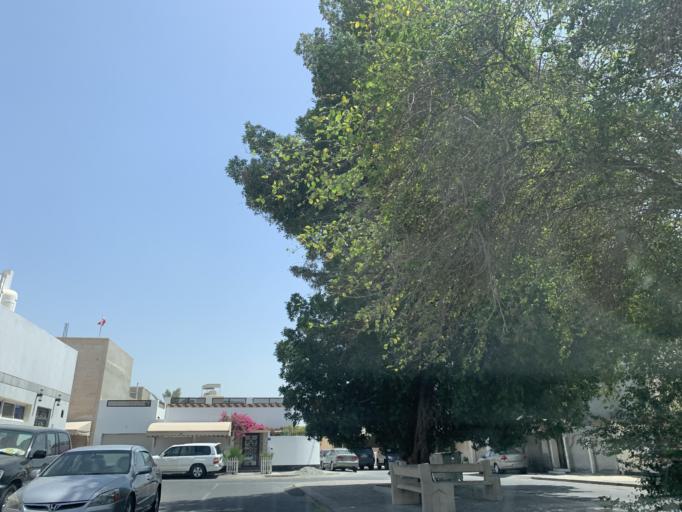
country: BH
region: Northern
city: Ar Rifa'
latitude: 26.1412
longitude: 50.5672
